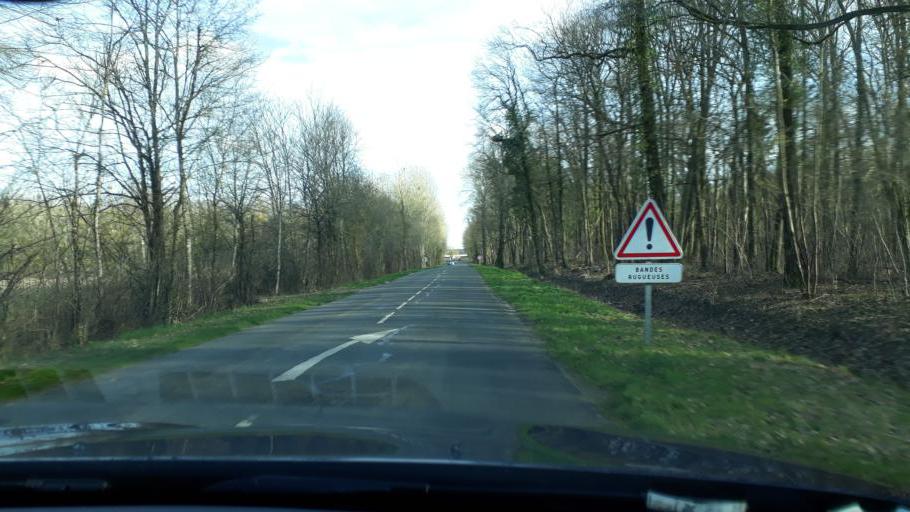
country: FR
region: Centre
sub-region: Departement du Loiret
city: Chilleurs-aux-Bois
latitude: 48.0619
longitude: 2.1585
